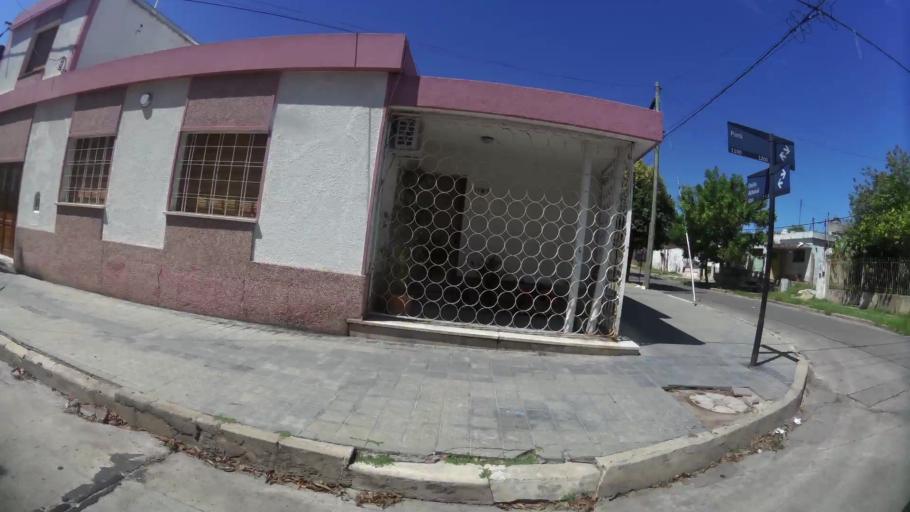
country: AR
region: Cordoba
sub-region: Departamento de Capital
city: Cordoba
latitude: -31.4258
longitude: -64.2056
